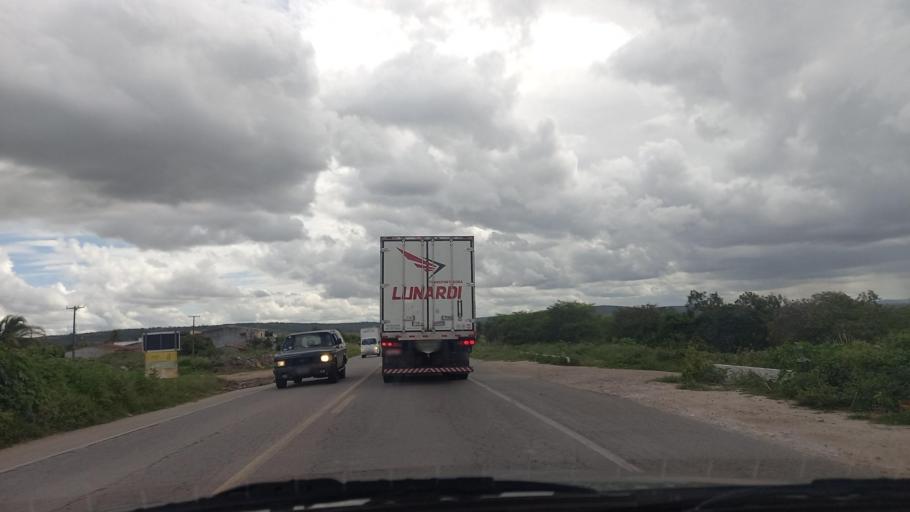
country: BR
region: Pernambuco
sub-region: Lajedo
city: Lajedo
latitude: -8.6614
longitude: -36.3431
